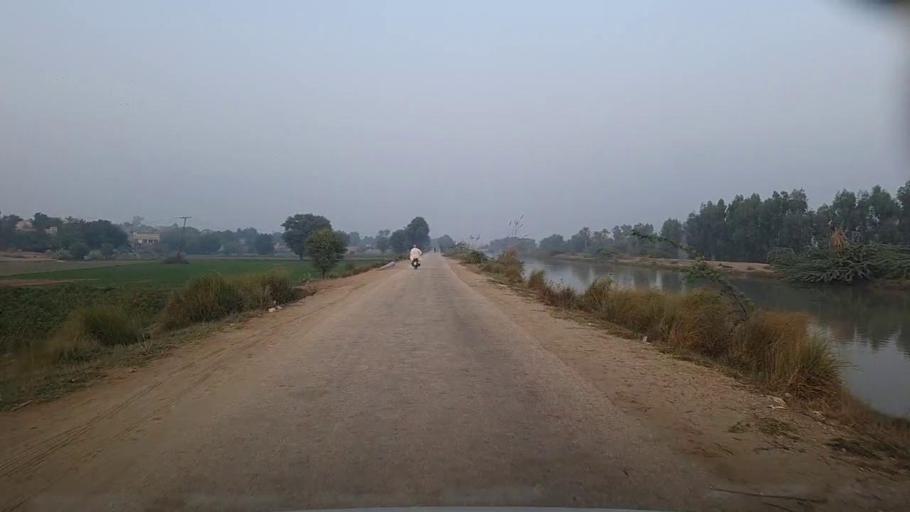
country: PK
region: Sindh
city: Bozdar
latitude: 27.0463
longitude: 68.5937
